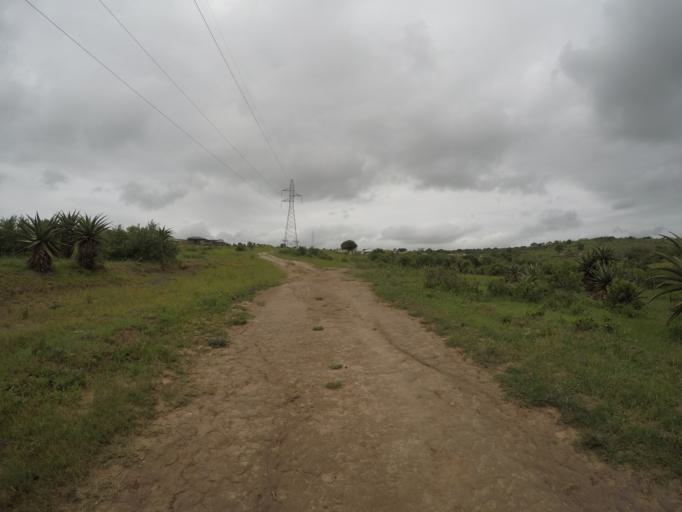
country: ZA
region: KwaZulu-Natal
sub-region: uThungulu District Municipality
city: Empangeni
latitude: -28.5985
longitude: 31.8453
